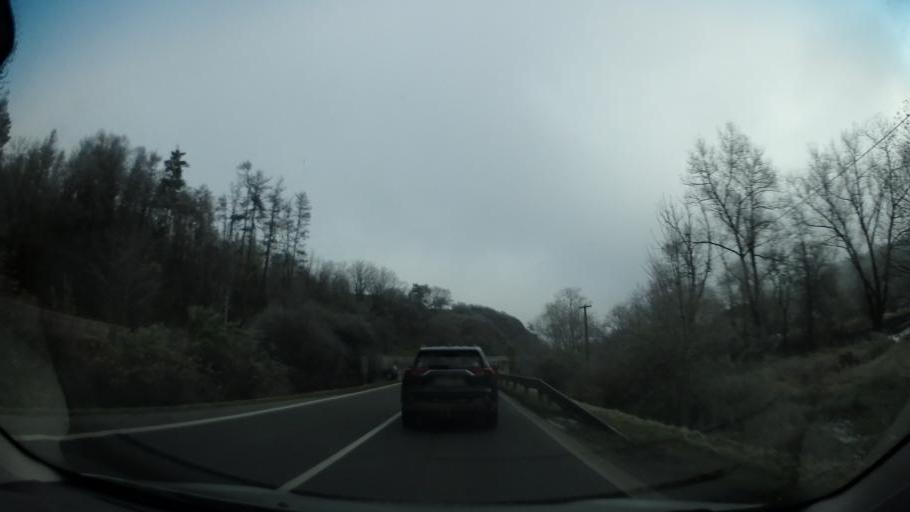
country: CZ
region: Vysocina
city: Vladislav
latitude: 49.2126
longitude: 15.9720
